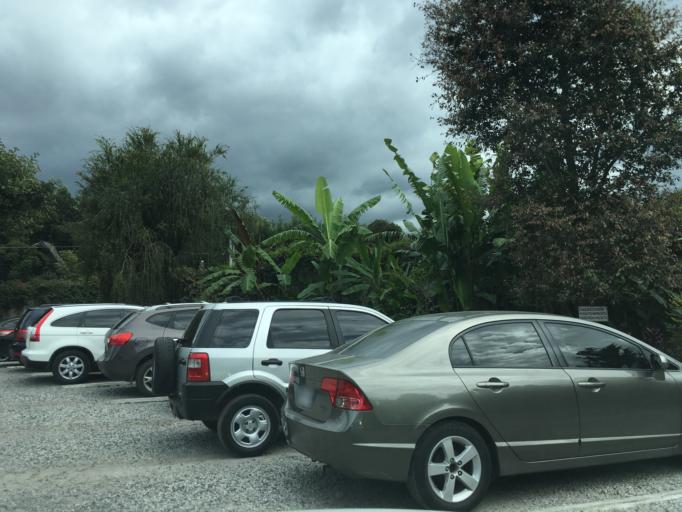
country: GT
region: Sacatepequez
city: Antigua Guatemala
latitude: 14.5498
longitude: -90.7346
